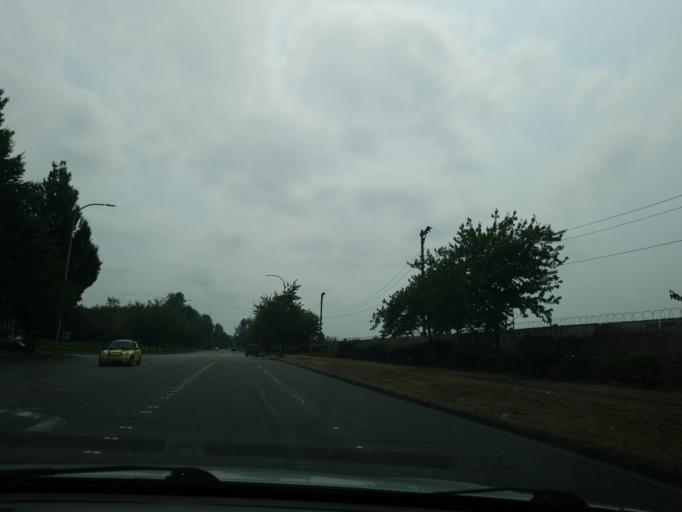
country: US
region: Washington
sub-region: King County
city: Renton
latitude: 47.4500
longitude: -122.2328
